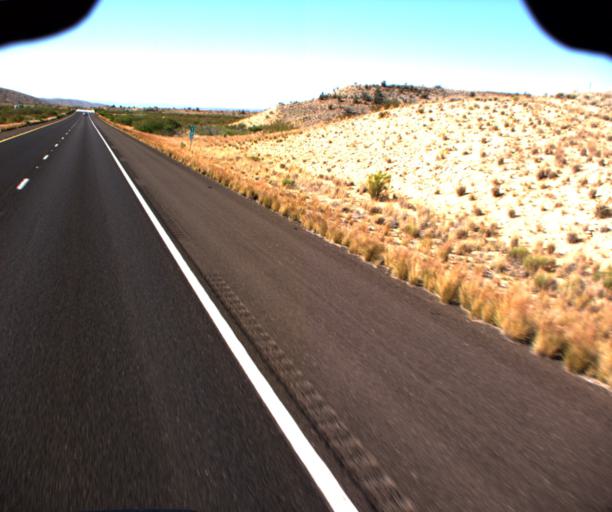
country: US
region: Arizona
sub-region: Mohave County
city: Kingman
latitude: 35.0419
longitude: -113.6652
